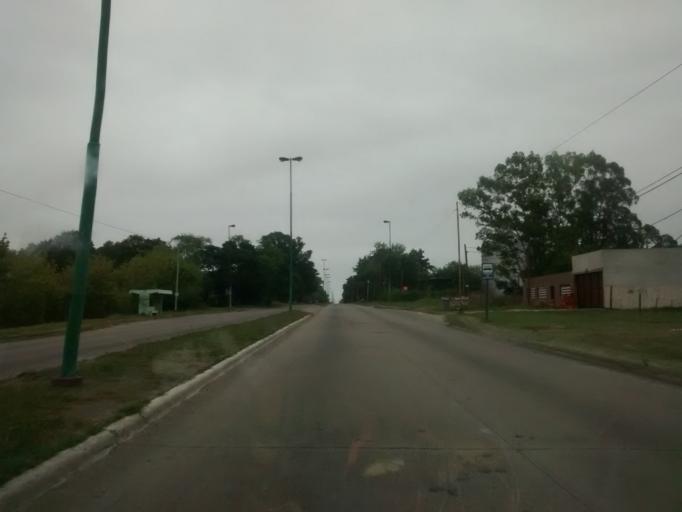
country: AR
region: Buenos Aires
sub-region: Partido de La Plata
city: La Plata
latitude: -34.9759
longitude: -58.0270
